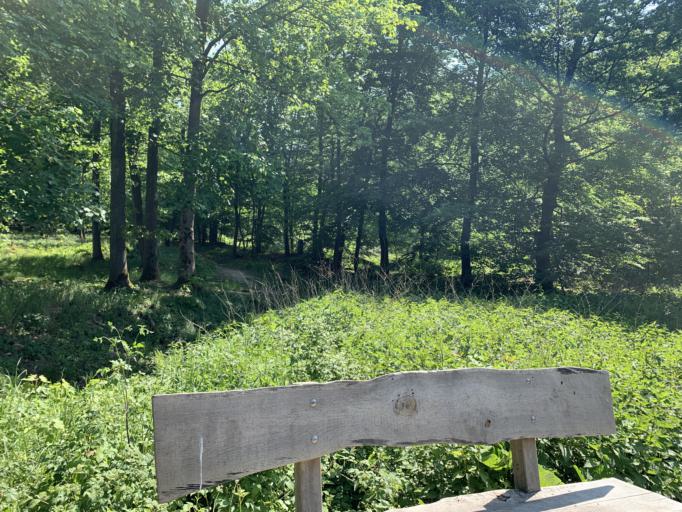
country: DE
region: North Rhine-Westphalia
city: Marl
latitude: 51.5976
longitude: 7.0757
